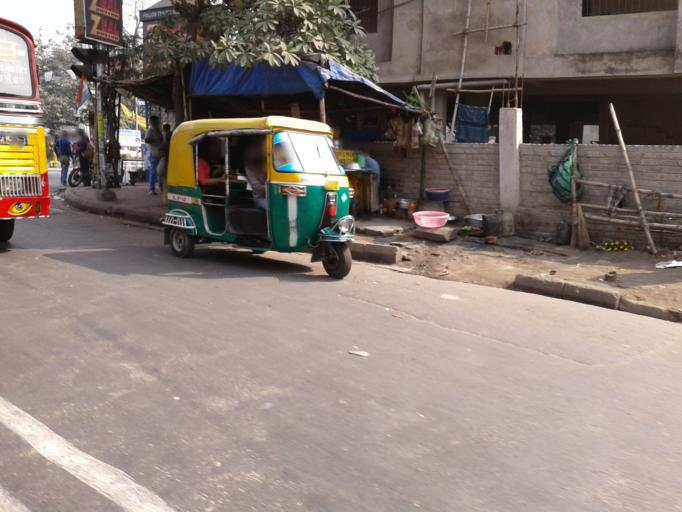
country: IN
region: West Bengal
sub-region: Kolkata
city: Kolkata
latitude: 22.5190
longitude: 88.3759
